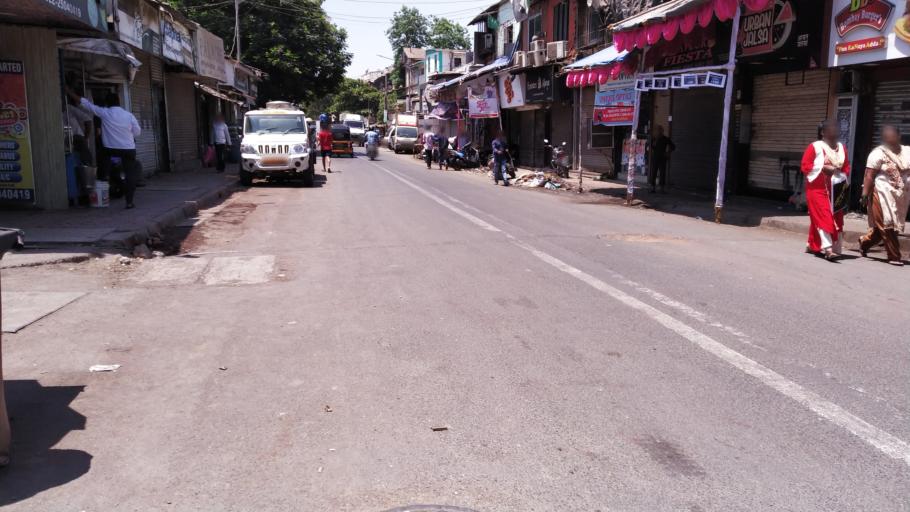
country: IN
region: Maharashtra
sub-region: Mumbai Suburban
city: Mumbai
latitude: 19.0791
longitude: 72.8803
